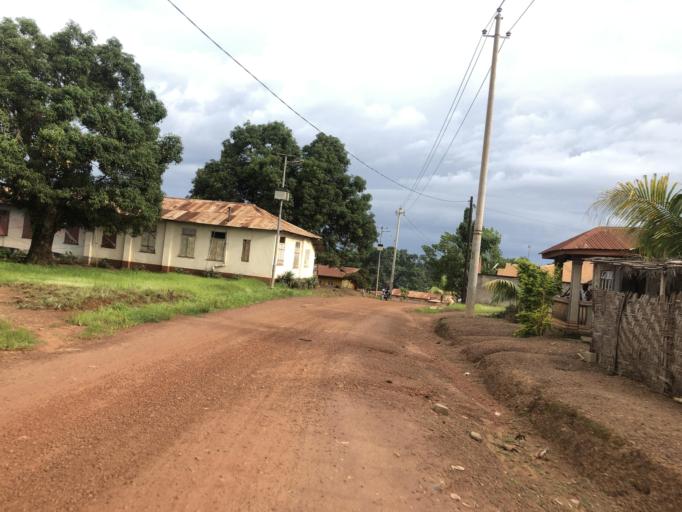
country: SL
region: Northern Province
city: Port Loko
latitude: 8.7627
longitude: -12.7814
